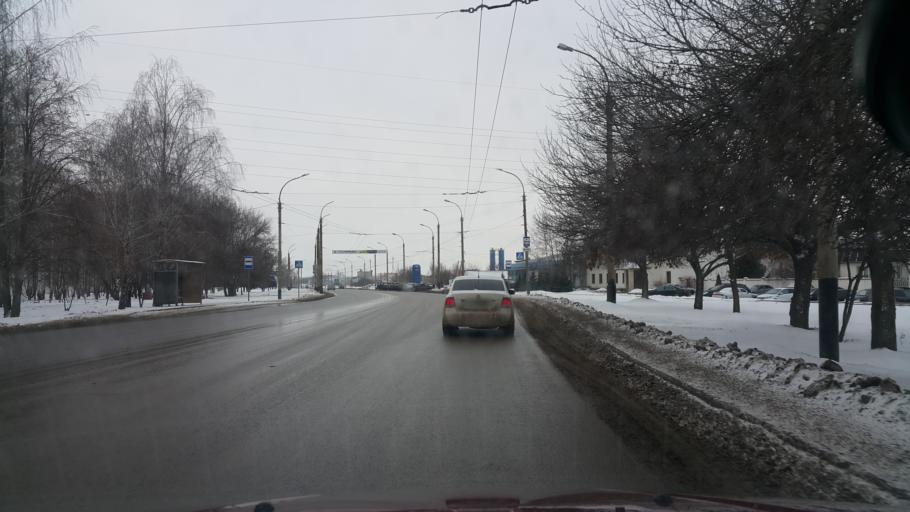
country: RU
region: Tambov
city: Tambov
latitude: 52.7358
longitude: 41.3882
